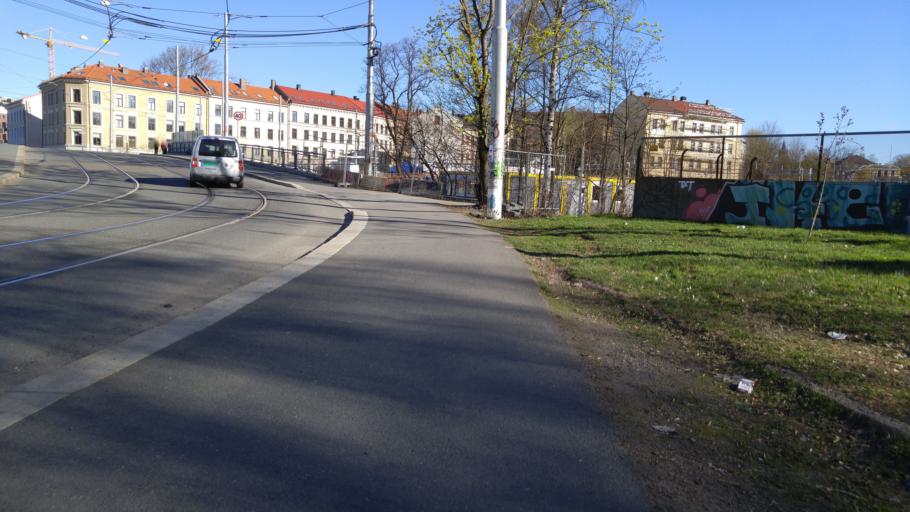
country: NO
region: Oslo
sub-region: Oslo
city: Oslo
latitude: 59.9035
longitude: 10.7673
